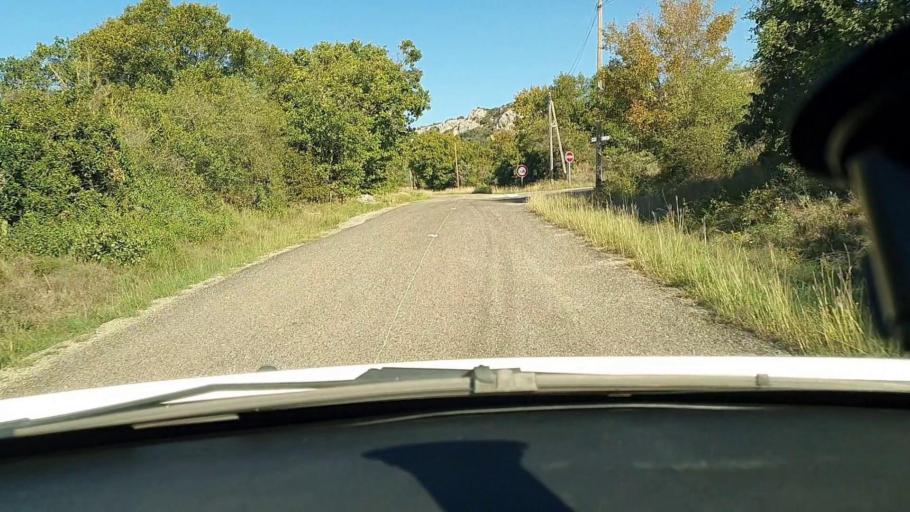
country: FR
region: Languedoc-Roussillon
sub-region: Departement du Gard
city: Barjac
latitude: 44.1904
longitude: 4.3225
